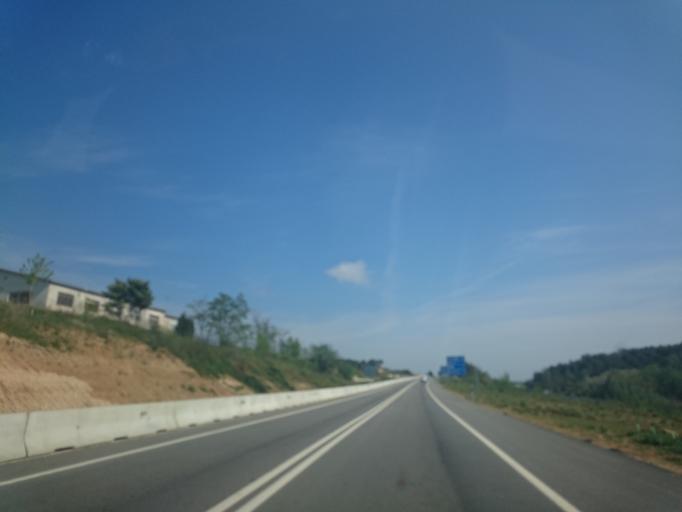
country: ES
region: Catalonia
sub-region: Provincia de Girona
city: Cervia de Ter
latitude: 42.0865
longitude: 2.8899
